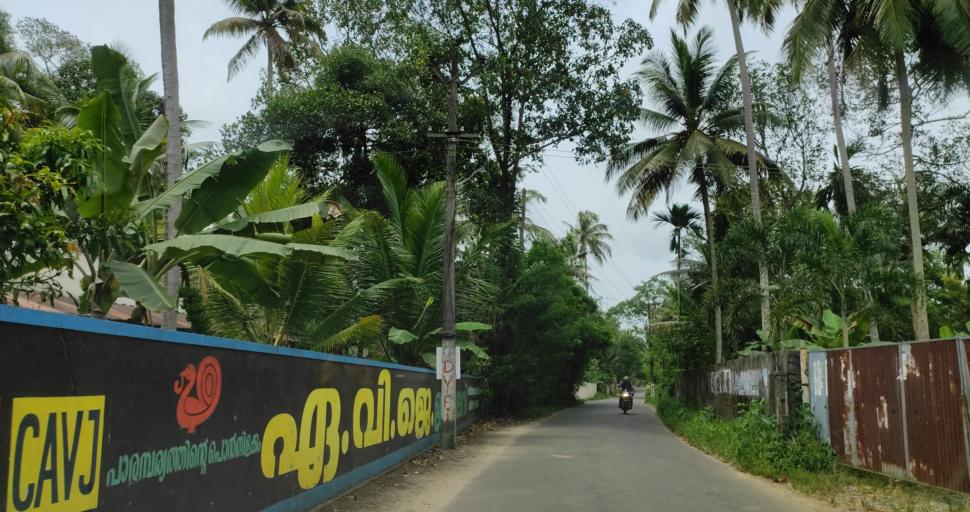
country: IN
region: Kerala
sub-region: Alappuzha
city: Shertallai
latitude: 9.6716
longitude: 76.3544
